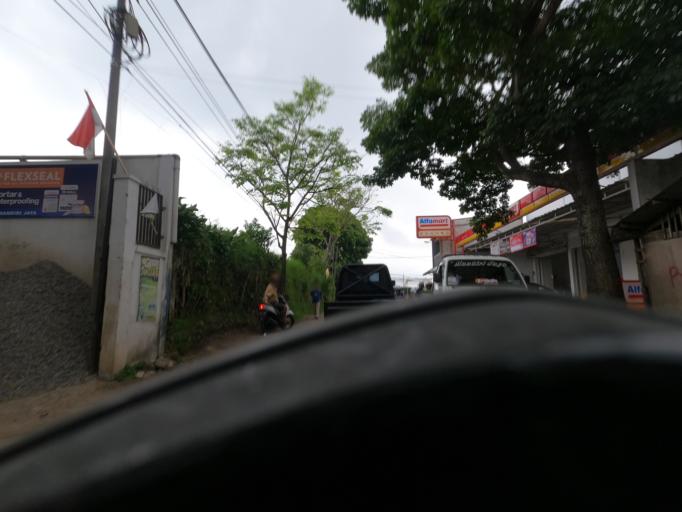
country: ID
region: West Java
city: Lembang
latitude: -6.8193
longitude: 107.6036
